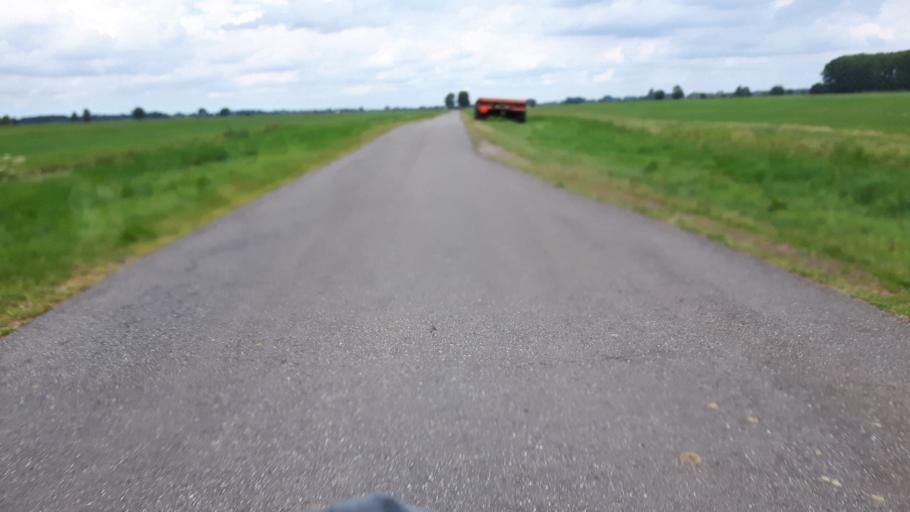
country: NL
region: South Holland
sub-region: Molenwaard
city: Nieuw-Lekkerland
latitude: 51.9111
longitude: 4.7259
